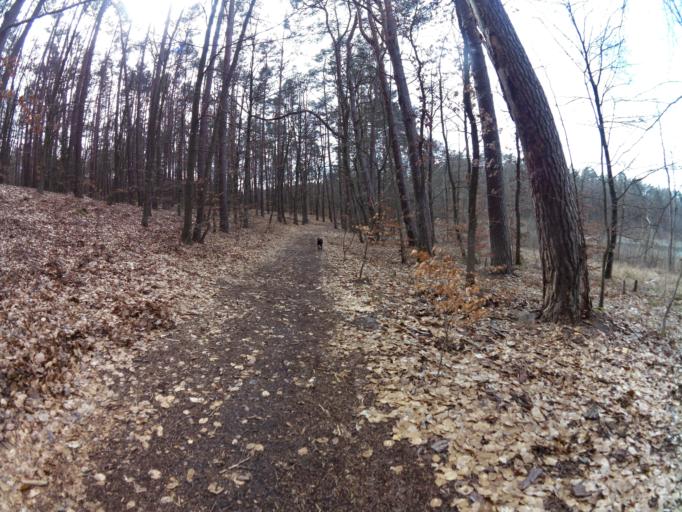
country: PL
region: West Pomeranian Voivodeship
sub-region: Powiat mysliborski
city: Mysliborz
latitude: 52.8436
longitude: 14.8396
